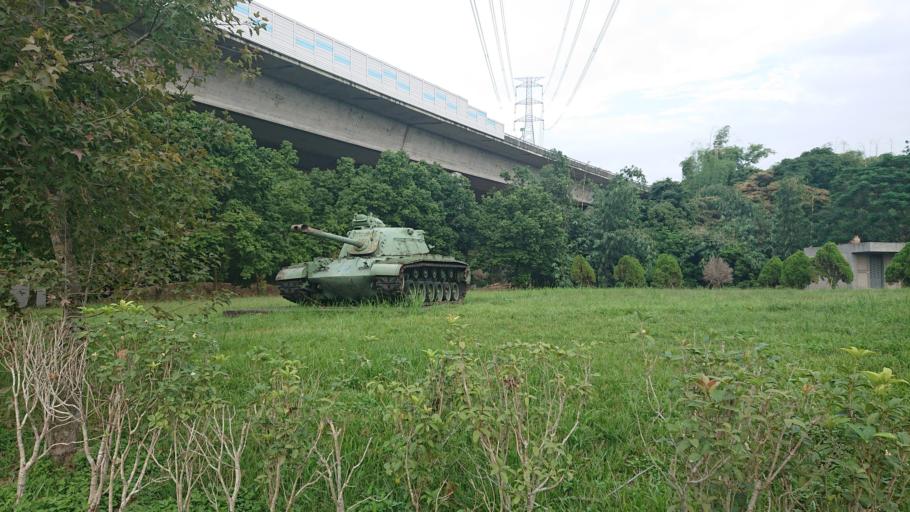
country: TW
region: Taiwan
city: Lugu
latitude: 23.7782
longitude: 120.6784
